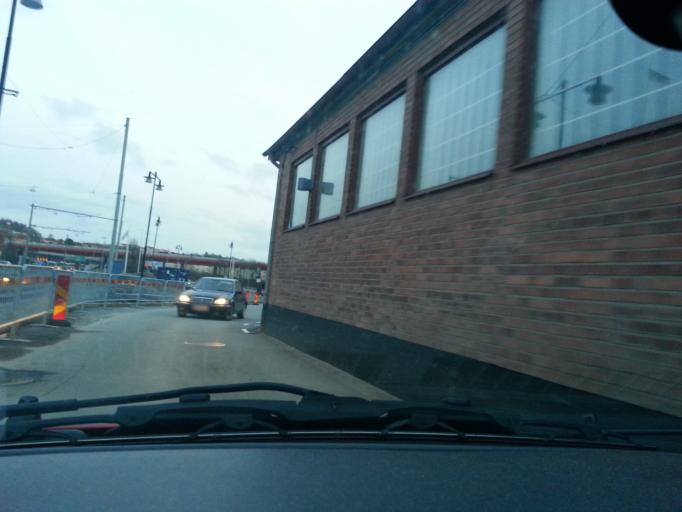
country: SE
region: Vaestra Goetaland
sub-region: Goteborg
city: Goeteborg
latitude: 57.7262
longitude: 12.0073
